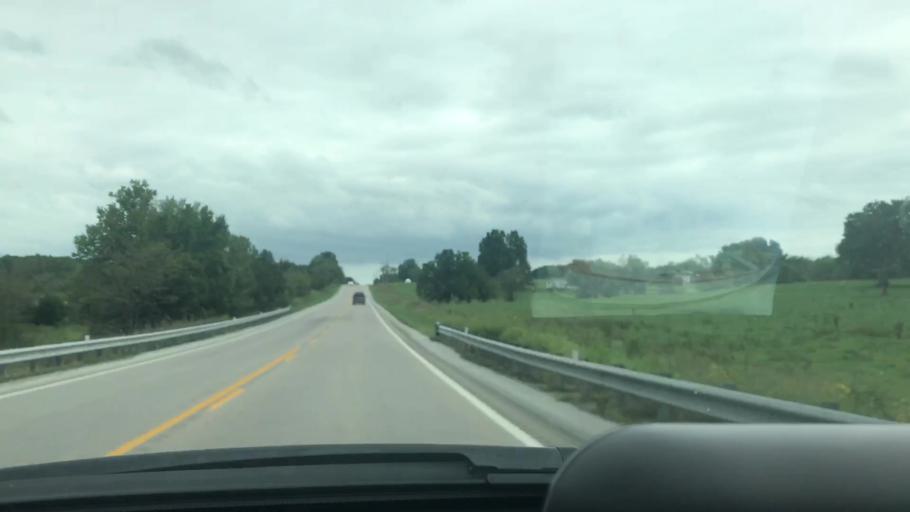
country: US
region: Missouri
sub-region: Dallas County
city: Buffalo
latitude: 37.7178
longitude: -93.1202
